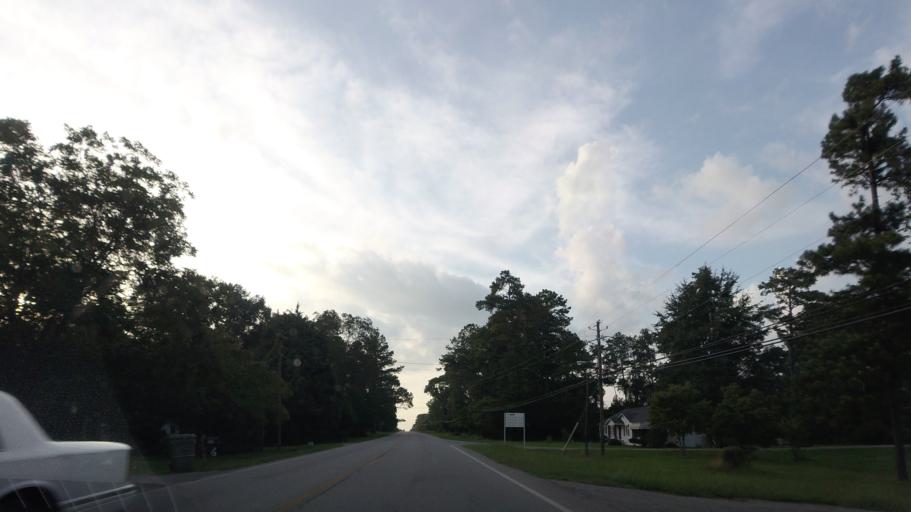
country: US
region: Georgia
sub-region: Wilkinson County
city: Gordon
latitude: 32.8860
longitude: -83.3468
